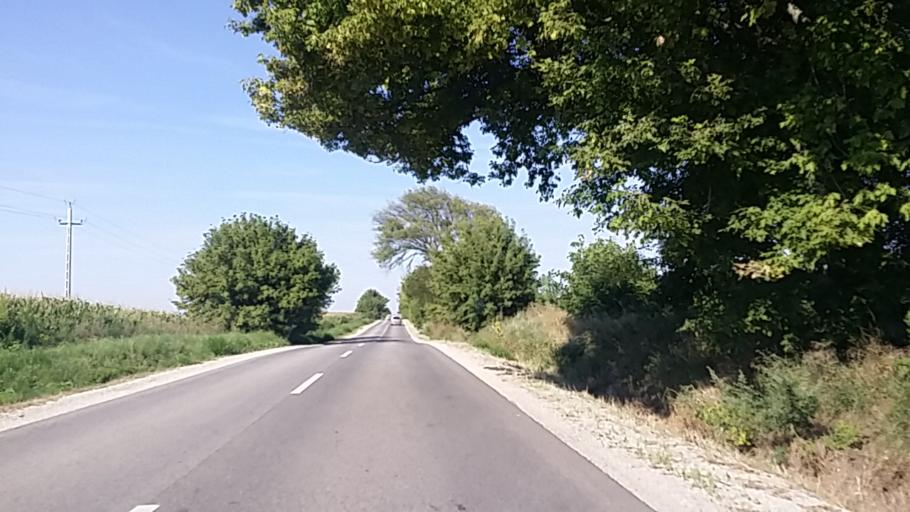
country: HU
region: Fejer
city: Pusztaszabolcs
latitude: 47.1098
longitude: 18.7489
